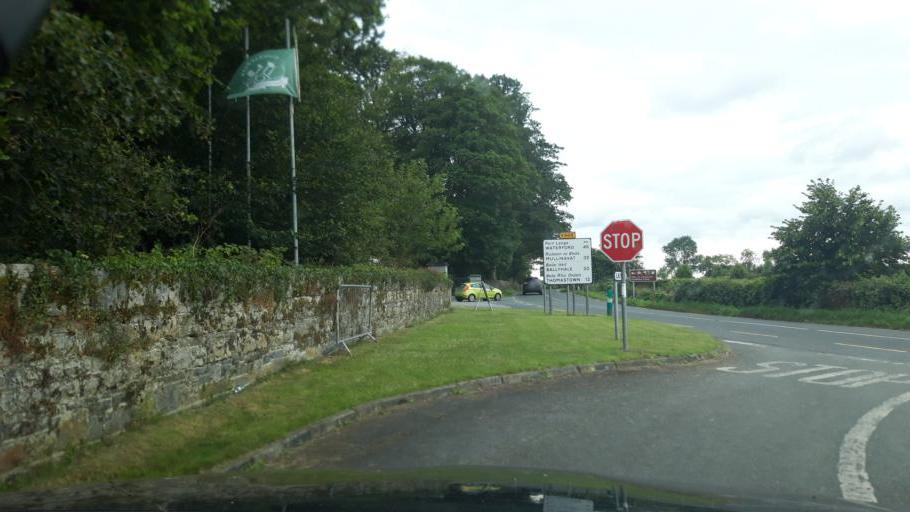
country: IE
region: Leinster
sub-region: Kilkenny
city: Thomastown
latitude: 52.6212
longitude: -7.0702
